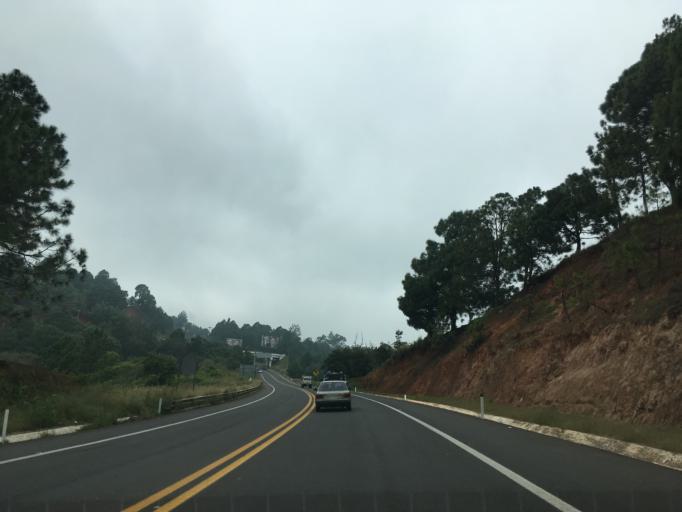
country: MX
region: Michoacan
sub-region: Uruapan
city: Toreo Bajo (El Toreo Bajo)
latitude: 19.4212
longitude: -101.9899
